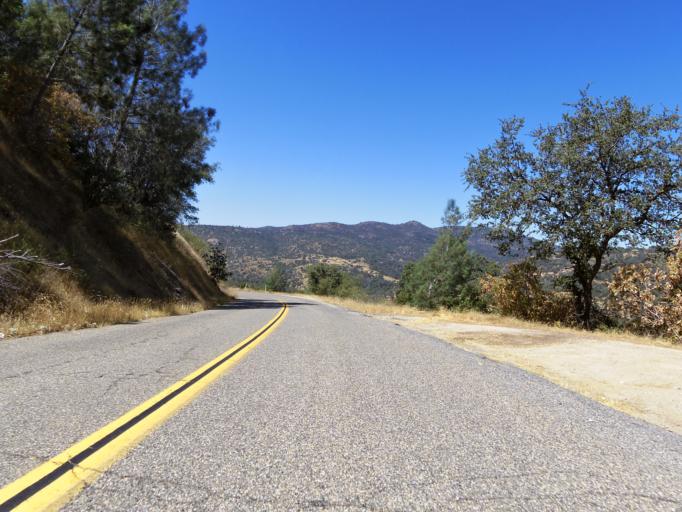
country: US
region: California
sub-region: Fresno County
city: Auberry
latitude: 37.1785
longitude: -119.5145
